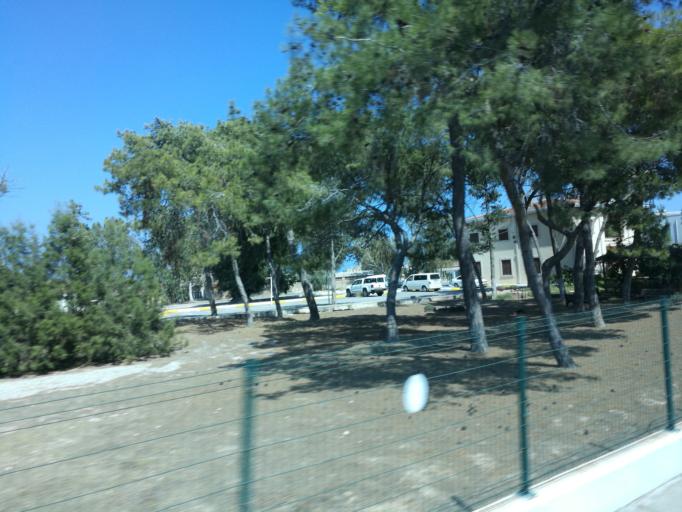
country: CY
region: Ammochostos
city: Famagusta
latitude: 35.1196
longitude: 33.9413
